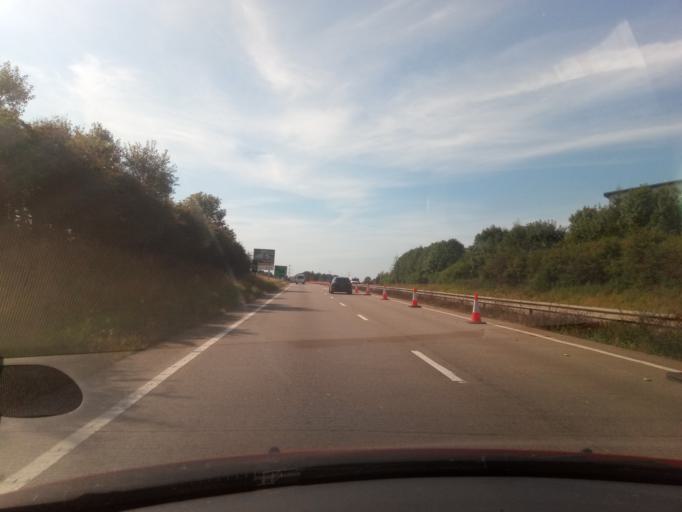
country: GB
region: England
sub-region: Stockton-on-Tees
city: Billingham
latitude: 54.6336
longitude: -1.3035
